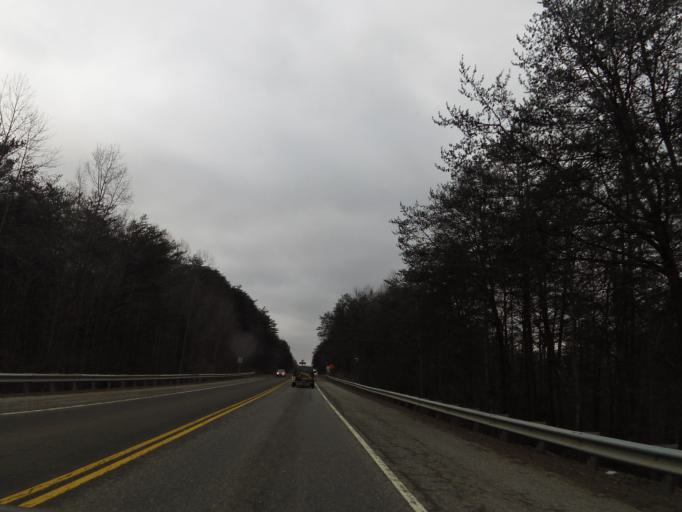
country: US
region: Tennessee
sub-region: Campbell County
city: Jacksboro
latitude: 36.3838
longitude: -84.2551
